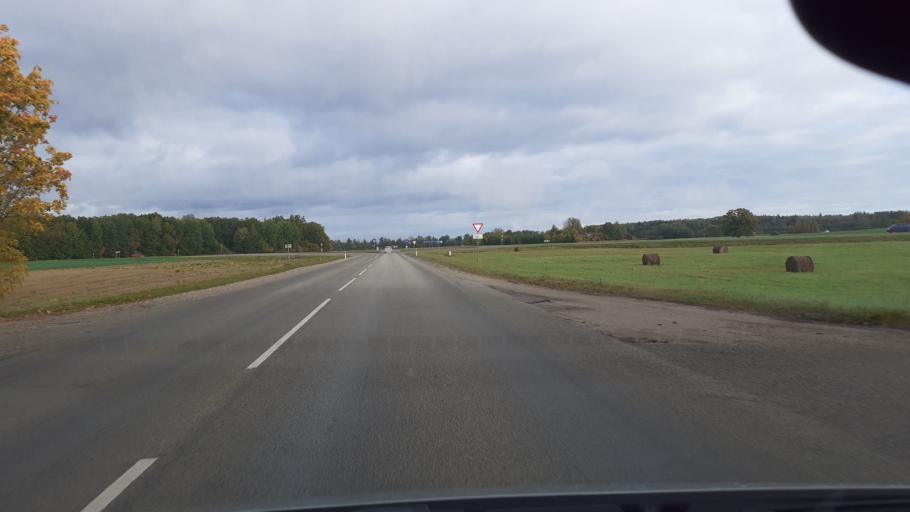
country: LV
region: Kuldigas Rajons
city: Kuldiga
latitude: 56.9825
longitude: 21.9312
